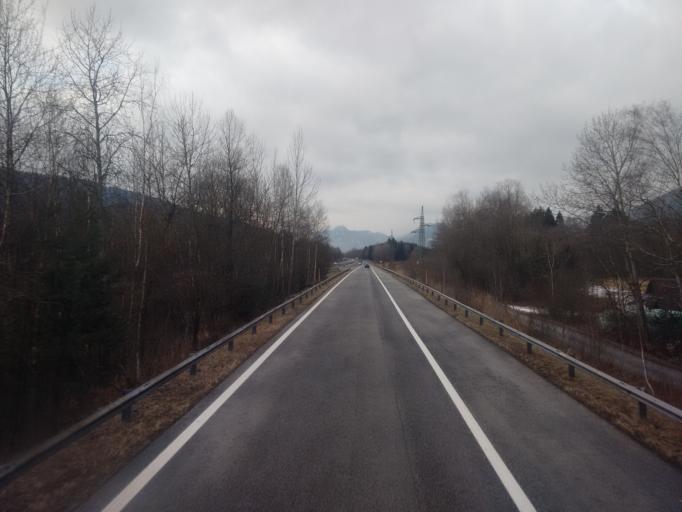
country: AT
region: Styria
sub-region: Politischer Bezirk Liezen
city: Selzthal
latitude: 47.5573
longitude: 14.2963
